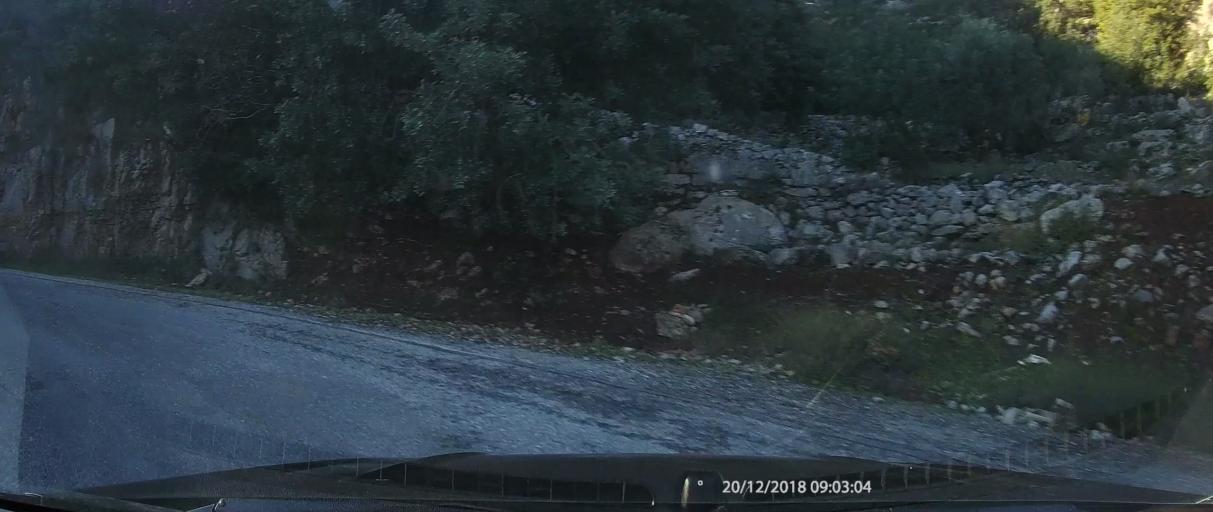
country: GR
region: Peloponnese
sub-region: Nomos Lakonias
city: Sykea
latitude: 36.9543
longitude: 22.9909
